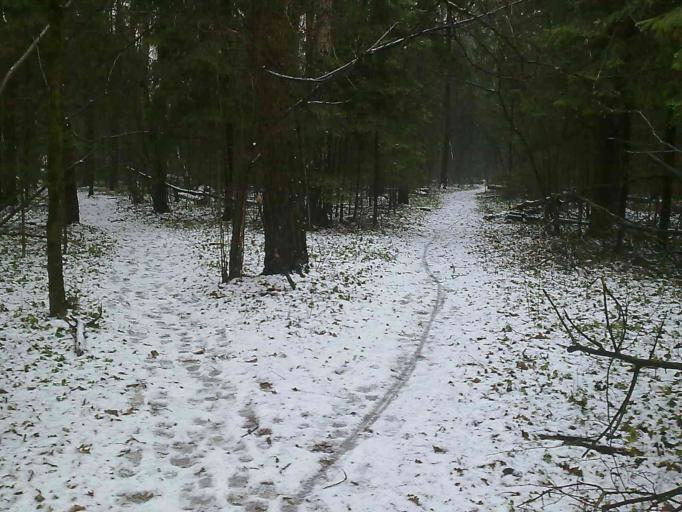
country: RU
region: Moskovskaya
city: Zhavoronki
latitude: 55.6617
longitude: 37.1550
